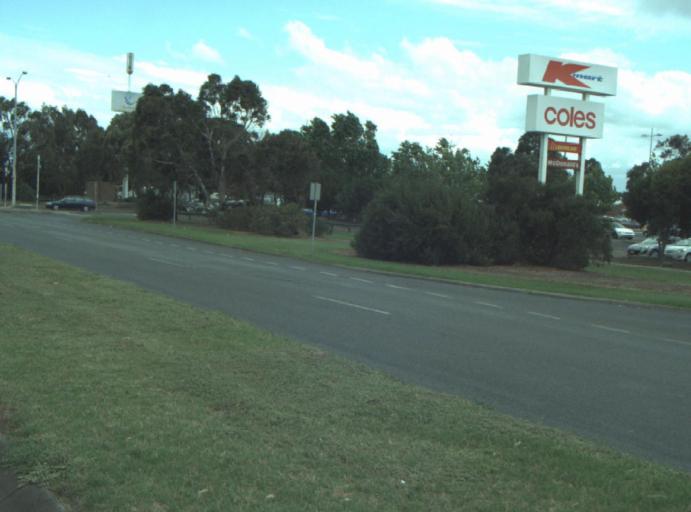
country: AU
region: Victoria
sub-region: Greater Geelong
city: Bell Park
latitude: -38.0753
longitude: 144.3586
